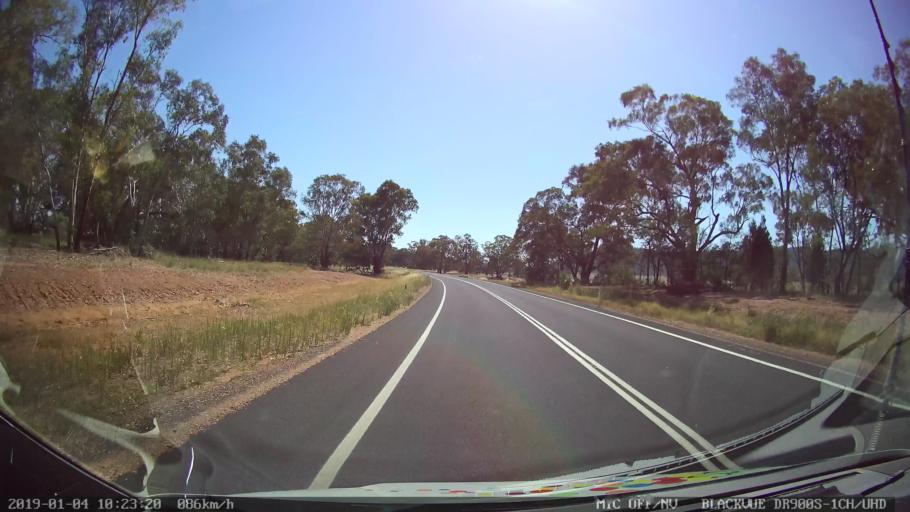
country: AU
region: New South Wales
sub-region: Cabonne
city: Canowindra
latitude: -33.3719
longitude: 148.5379
